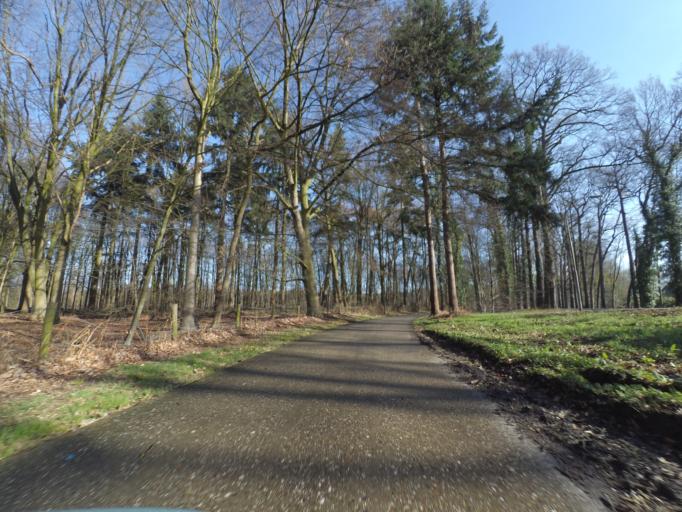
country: NL
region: Gelderland
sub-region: Gemeente Barneveld
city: Barneveld
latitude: 52.1433
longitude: 5.5987
